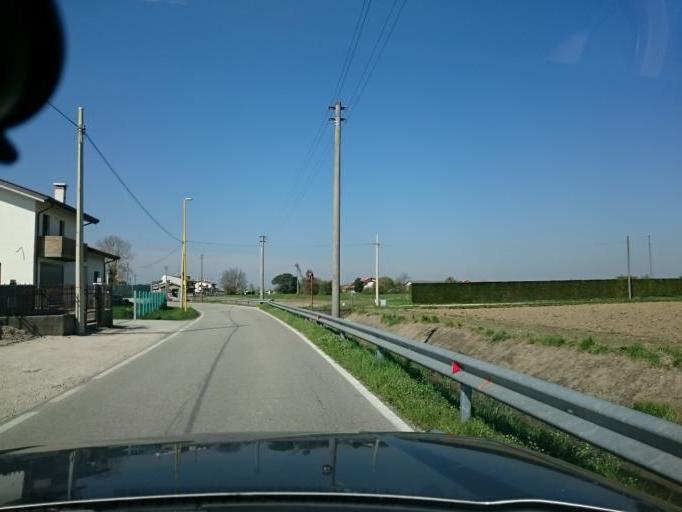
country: IT
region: Veneto
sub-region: Provincia di Padova
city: Ponte San Nicolo
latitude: 45.3663
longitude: 11.9038
